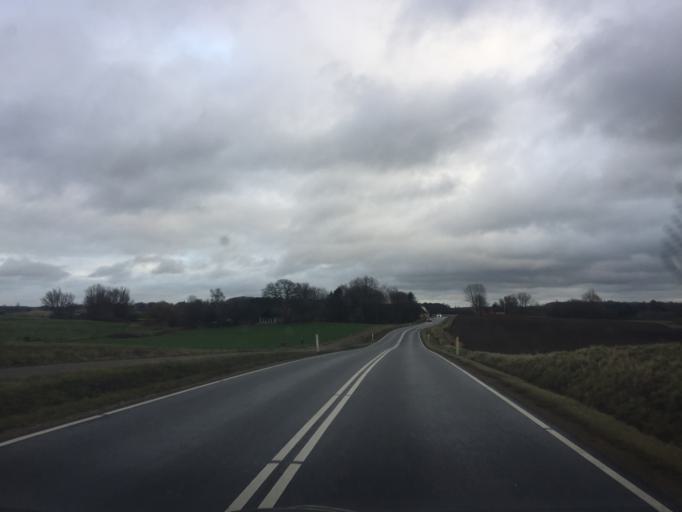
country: DK
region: Zealand
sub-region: Holbaek Kommune
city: Tollose
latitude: 55.6082
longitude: 11.7221
